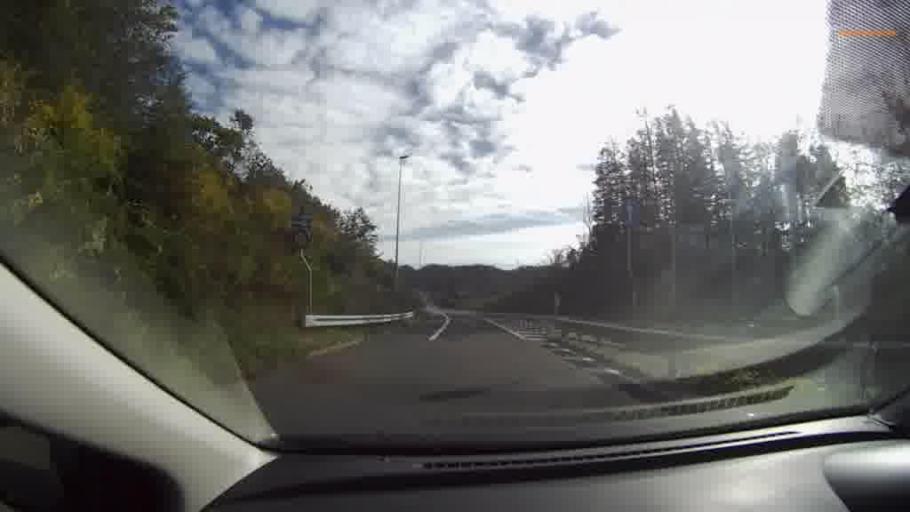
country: JP
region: Hokkaido
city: Kushiro
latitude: 43.0795
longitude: 143.9630
